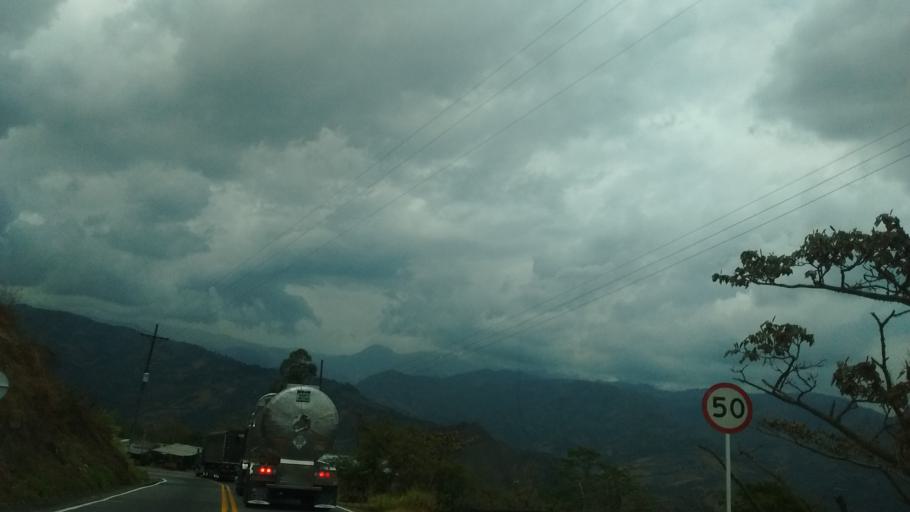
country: CO
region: Cauca
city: Rosas
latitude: 2.2958
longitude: -76.7089
